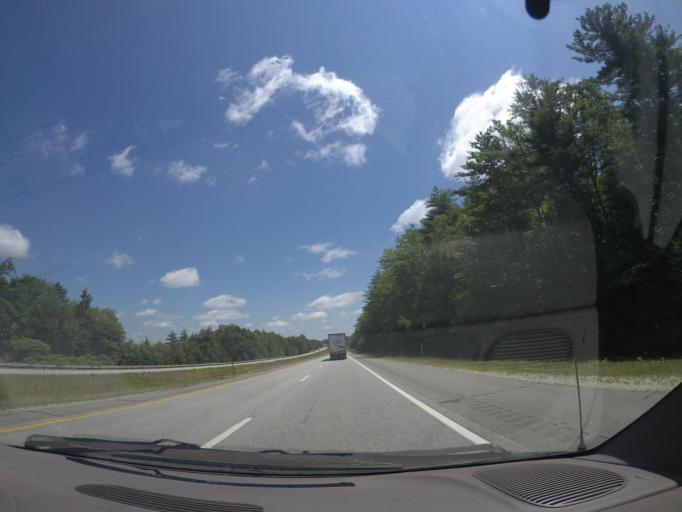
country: US
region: New Hampshire
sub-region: Rockingham County
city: Raymond
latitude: 43.0227
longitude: -71.2105
